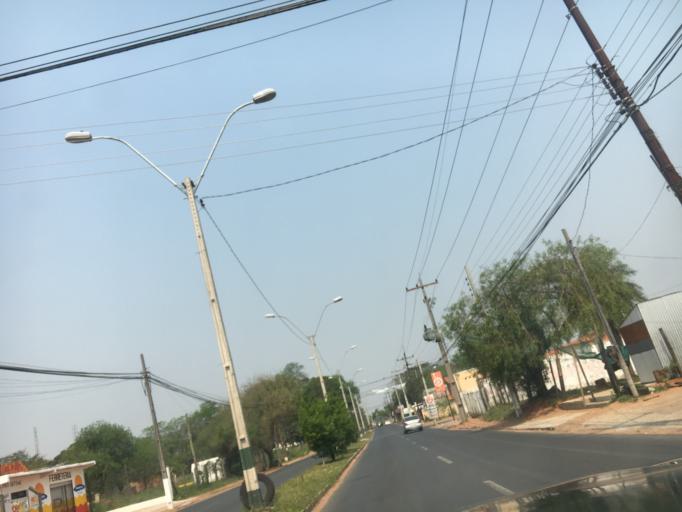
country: PY
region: Central
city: Villa Elisa
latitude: -25.3838
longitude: -57.5844
